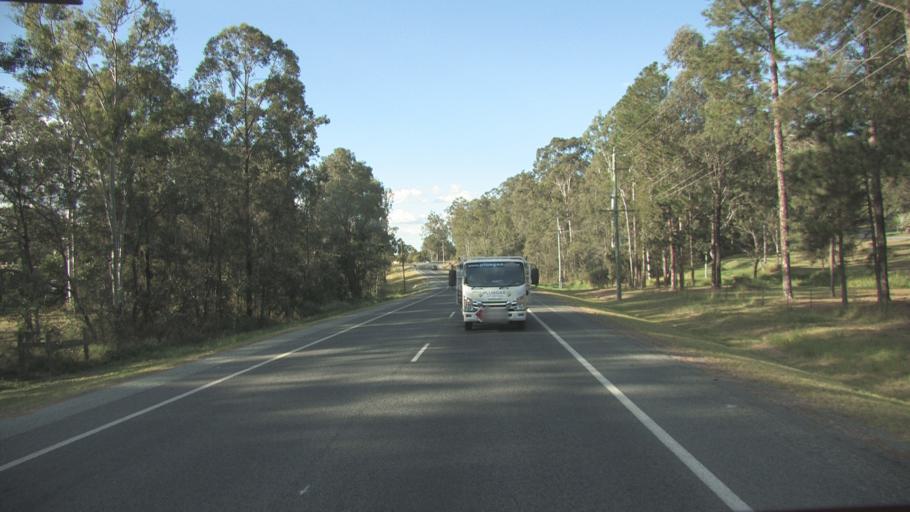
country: AU
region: Queensland
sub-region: Ipswich
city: Springfield Lakes
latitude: -27.7226
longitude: 152.9600
